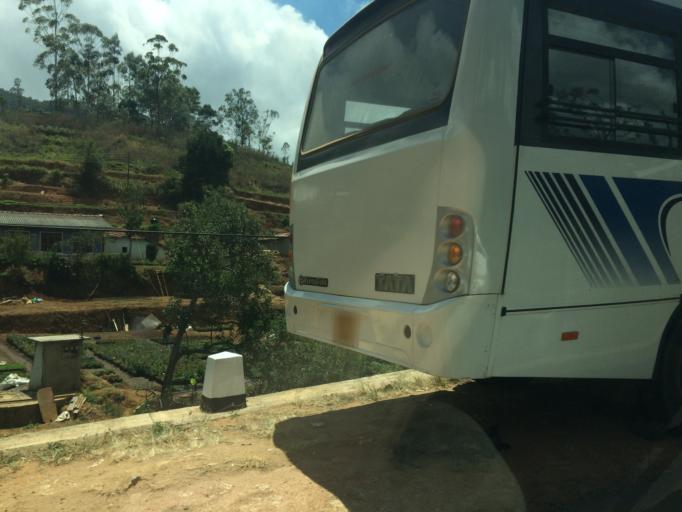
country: LK
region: Central
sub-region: Nuwara Eliya District
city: Nuwara Eliya
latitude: 6.9061
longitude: 80.8489
